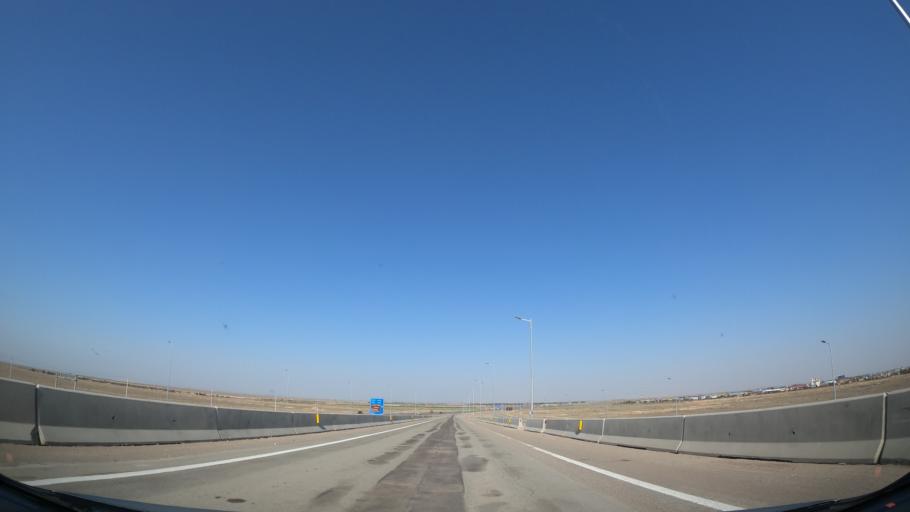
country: IR
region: Tehran
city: Eqbaliyeh
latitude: 35.1346
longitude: 51.5188
